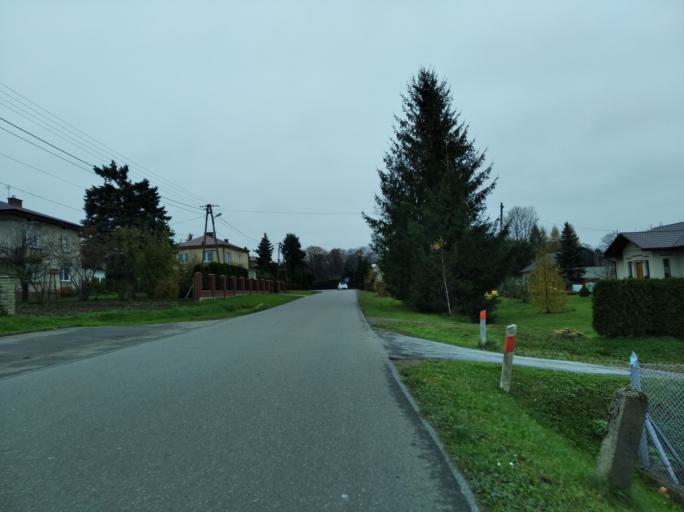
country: PL
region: Subcarpathian Voivodeship
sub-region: Powiat krosnienski
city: Jedlicze
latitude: 49.6893
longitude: 21.6686
